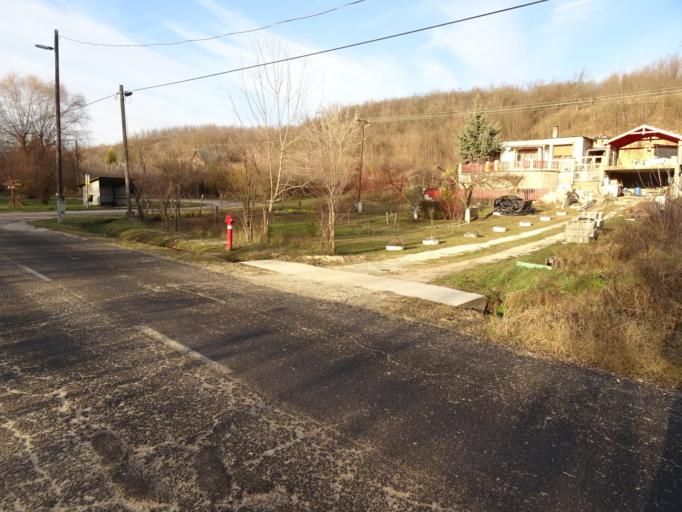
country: HU
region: Pest
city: Mende
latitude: 47.4073
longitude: 19.4812
